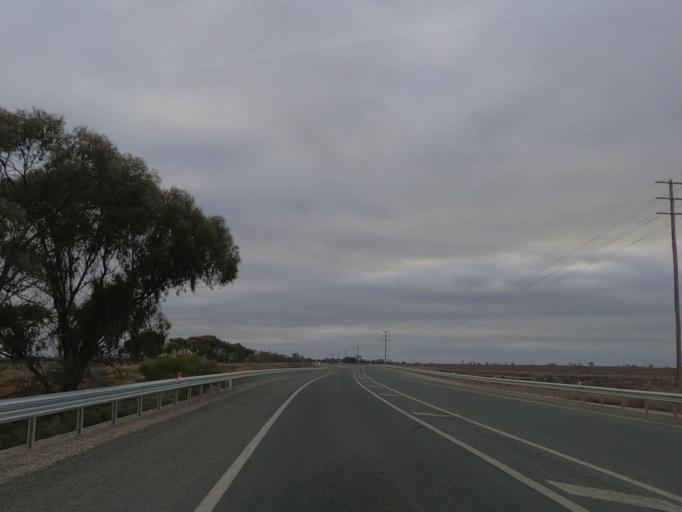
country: AU
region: Victoria
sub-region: Swan Hill
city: Swan Hill
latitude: -35.5445
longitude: 143.7585
